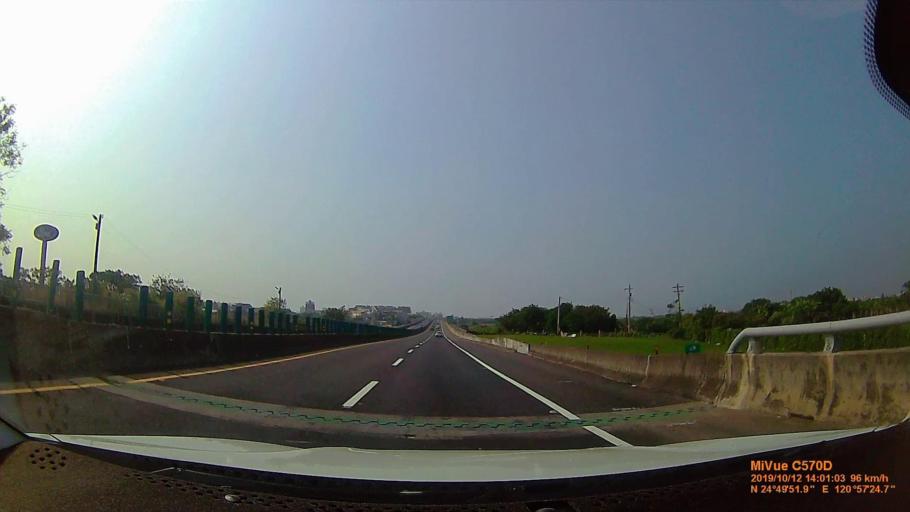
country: TW
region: Taiwan
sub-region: Hsinchu
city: Hsinchu
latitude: 24.8312
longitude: 120.9568
